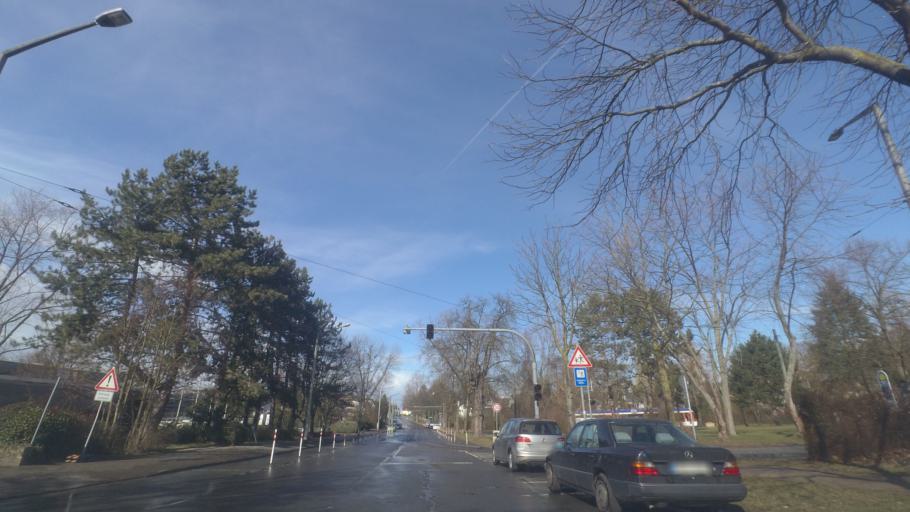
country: DE
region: Hesse
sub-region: Regierungsbezirk Darmstadt
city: Darmstadt
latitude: 49.8501
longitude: 8.6533
